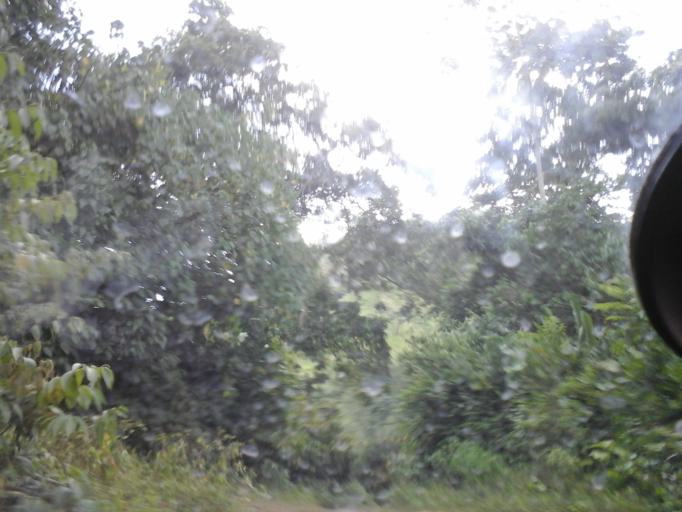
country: CO
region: Cesar
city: Manaure Balcon del Cesar
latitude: 10.2948
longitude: -73.0738
